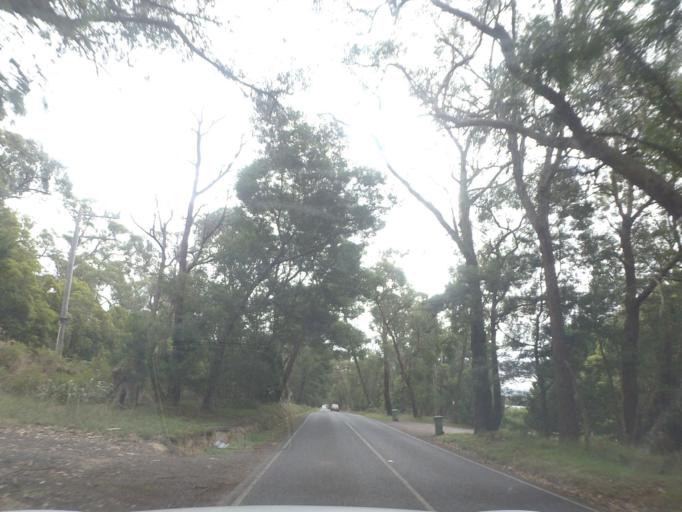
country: AU
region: Victoria
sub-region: Maroondah
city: Kilsyth South
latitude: -37.8299
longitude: 145.3250
